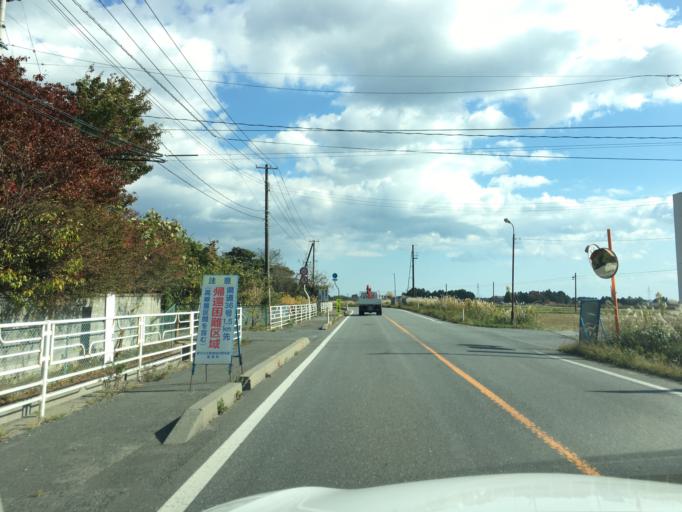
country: JP
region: Fukushima
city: Namie
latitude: 37.3688
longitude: 140.9799
